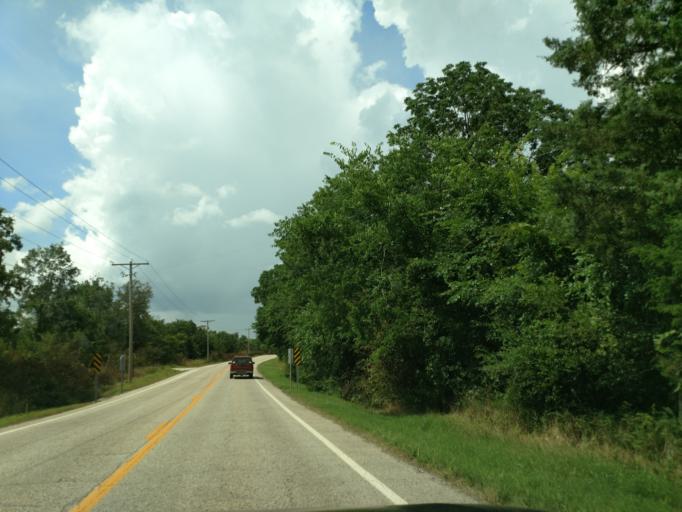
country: US
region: Arkansas
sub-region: Boone County
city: Harrison
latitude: 36.2805
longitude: -93.2351
